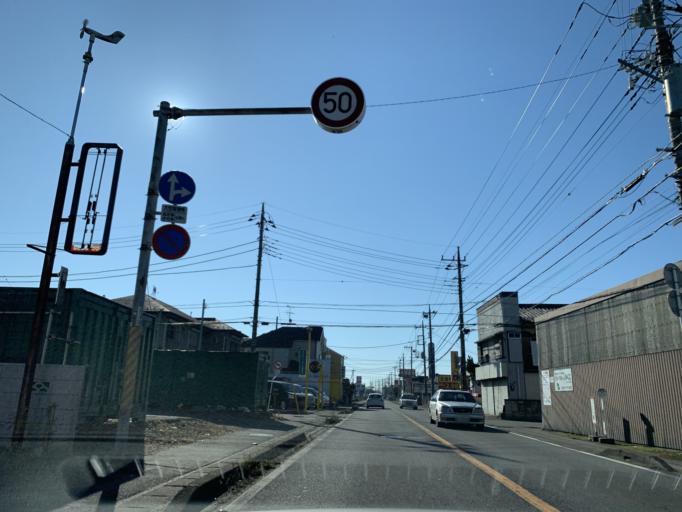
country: JP
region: Chiba
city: Matsudo
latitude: 35.8086
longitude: 139.8951
